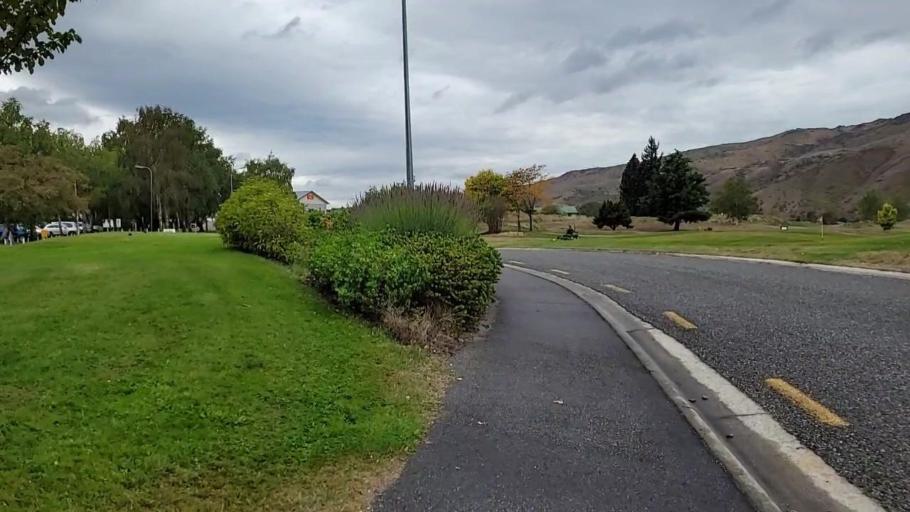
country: NZ
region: Otago
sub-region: Queenstown-Lakes District
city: Wanaka
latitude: -45.0408
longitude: 169.2076
